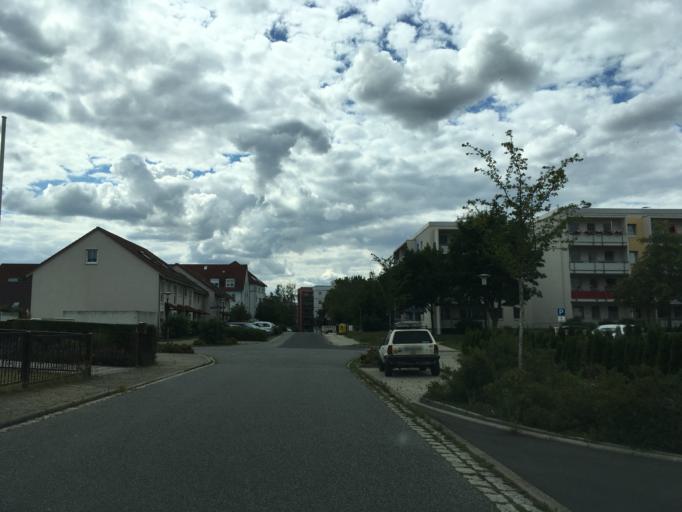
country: DE
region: Saxony
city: Radeberg
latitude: 51.1044
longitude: 13.9202
